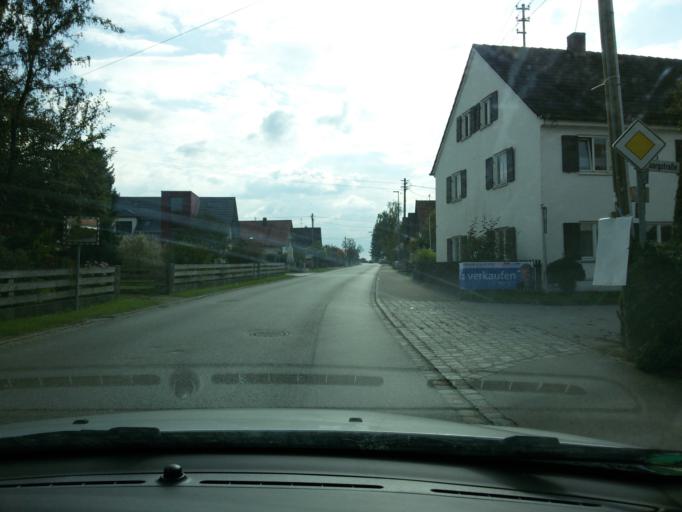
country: DE
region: Bavaria
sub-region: Swabia
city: Lamerdingen
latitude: 48.0893
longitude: 10.7400
